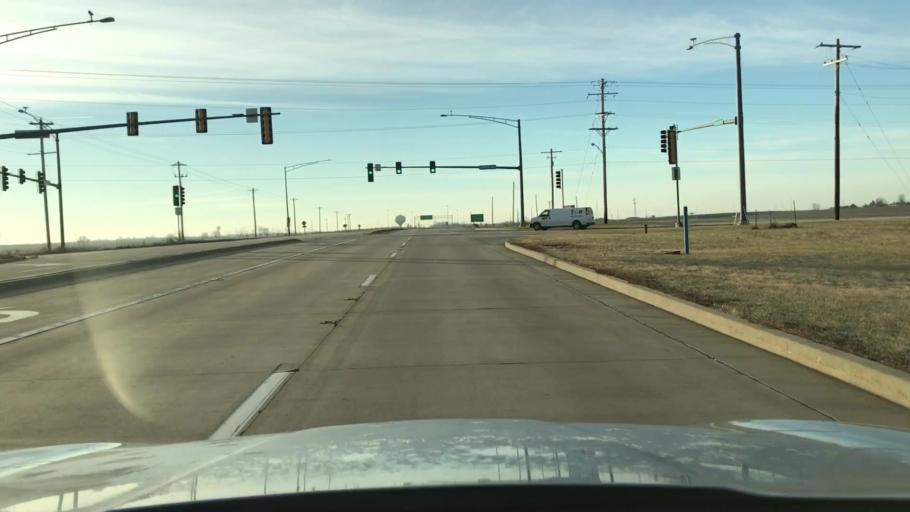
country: US
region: Illinois
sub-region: McLean County
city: Normal
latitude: 40.5476
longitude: -88.9444
